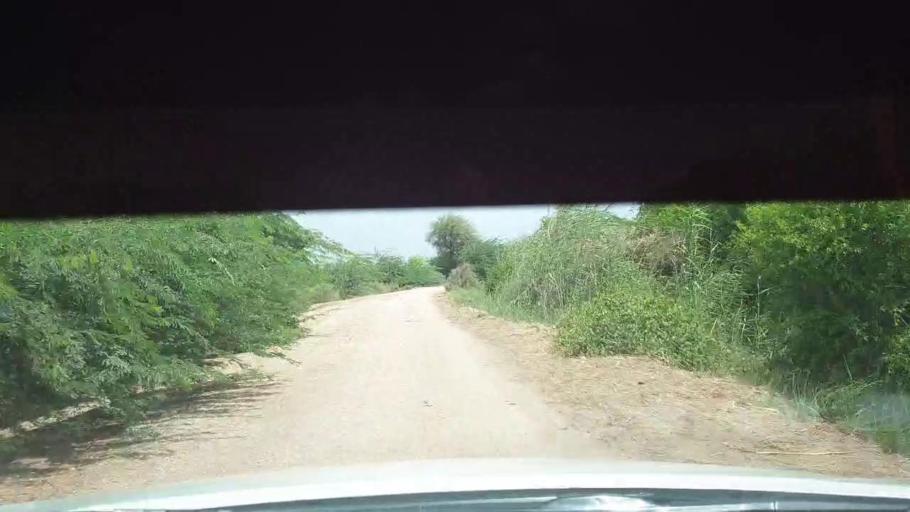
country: PK
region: Sindh
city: Kadhan
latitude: 24.5101
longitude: 68.9766
